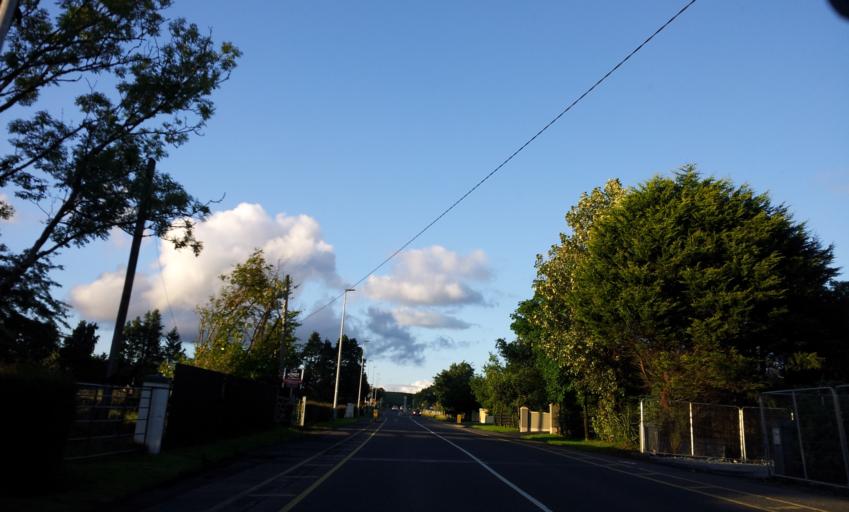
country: IE
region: Munster
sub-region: County Limerick
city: Newcastle West
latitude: 52.3993
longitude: -9.1723
